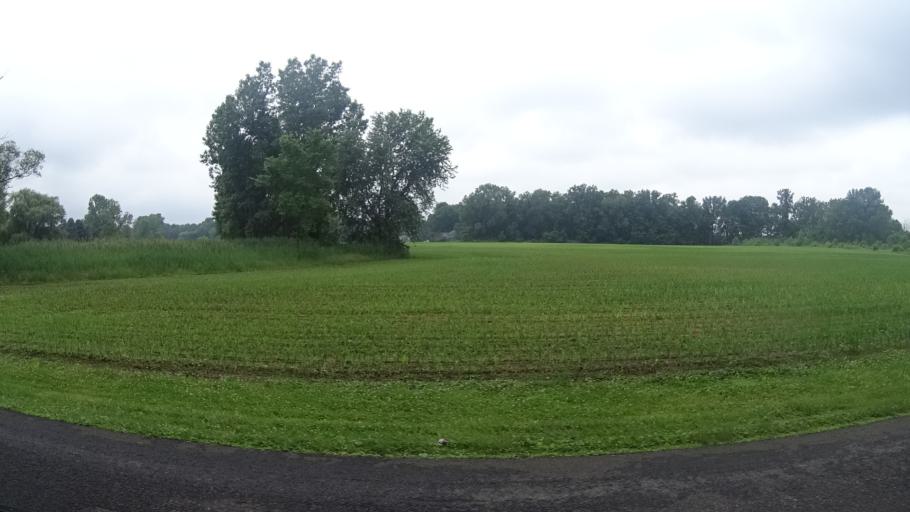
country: US
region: Ohio
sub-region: Erie County
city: Milan
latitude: 41.2901
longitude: -82.5348
